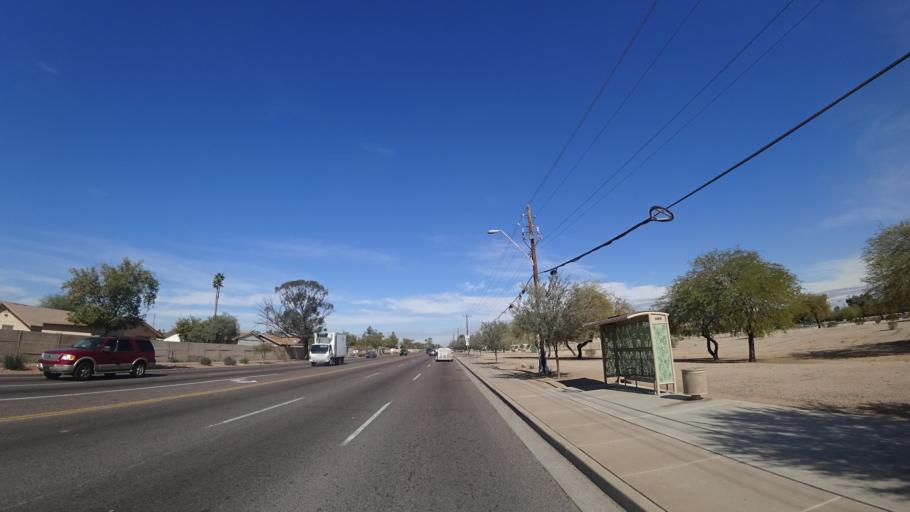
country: US
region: Arizona
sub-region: Maricopa County
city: Tolleson
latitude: 33.4733
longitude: -112.2032
